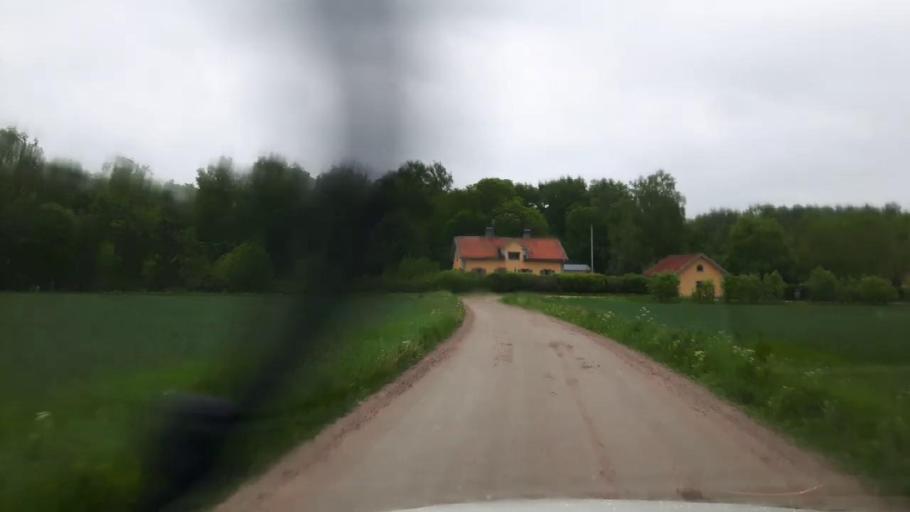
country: SE
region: Vaestmanland
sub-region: Arboga Kommun
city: Tyringe
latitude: 59.3817
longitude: 15.9356
